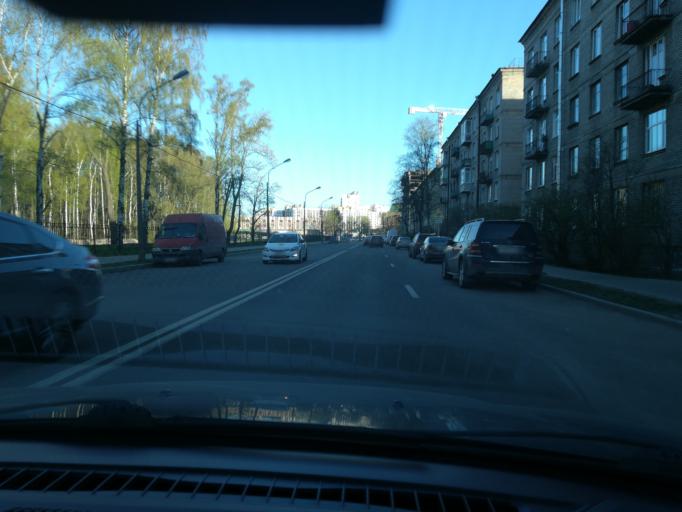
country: RU
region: St.-Petersburg
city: Vasyl'evsky Ostrov
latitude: 59.9408
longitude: 30.2421
